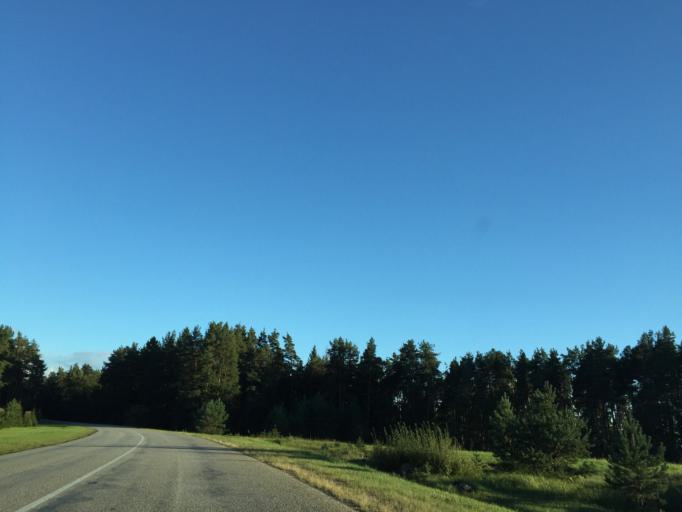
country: LV
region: Kuldigas Rajons
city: Kuldiga
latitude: 56.9138
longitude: 22.0560
